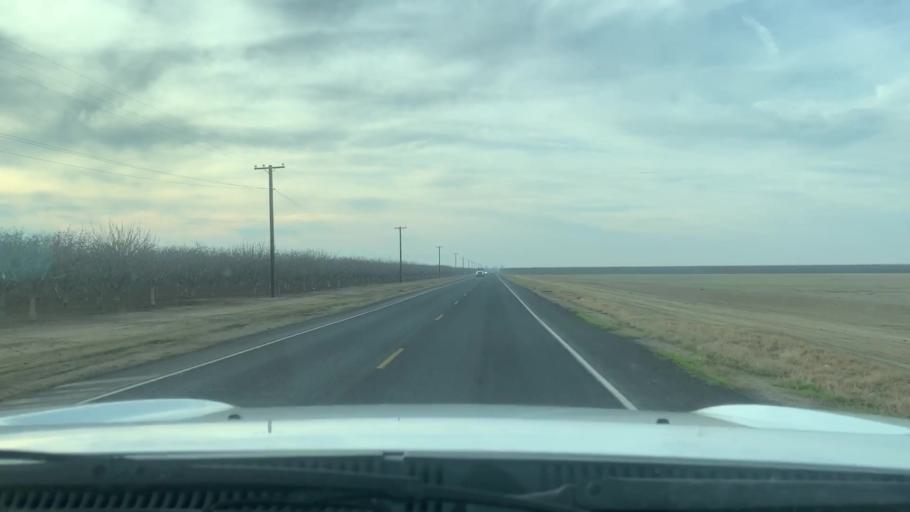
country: US
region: California
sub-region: Kern County
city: Lost Hills
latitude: 35.4994
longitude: -119.6231
